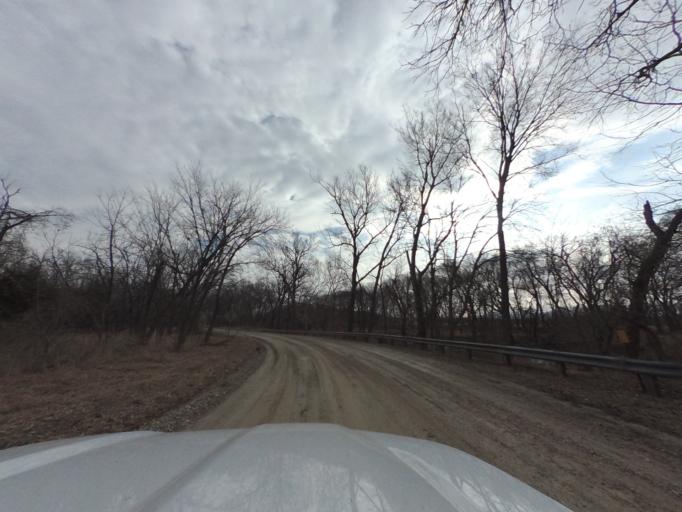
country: US
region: Kansas
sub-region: Chase County
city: Cottonwood Falls
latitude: 38.2995
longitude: -96.7408
